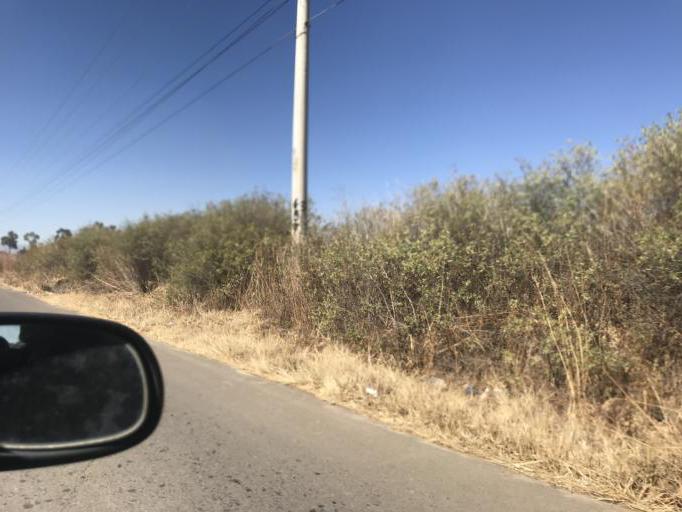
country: BO
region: Cochabamba
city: Tarata
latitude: -17.6055
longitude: -65.9941
